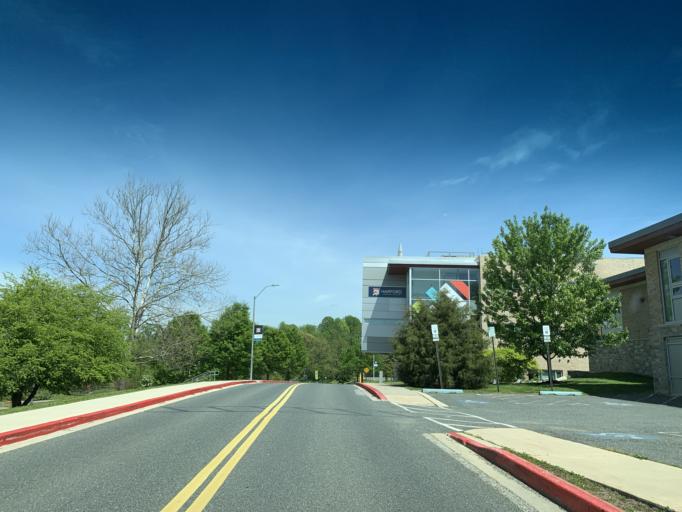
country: US
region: Maryland
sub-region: Harford County
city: South Bel Air
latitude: 39.5622
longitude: -76.2821
